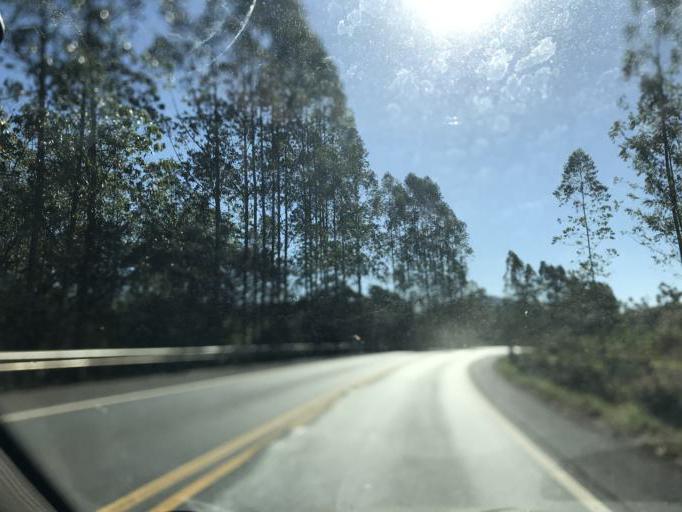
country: BR
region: Minas Gerais
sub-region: Bambui
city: Bambui
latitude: -19.8216
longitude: -46.0186
